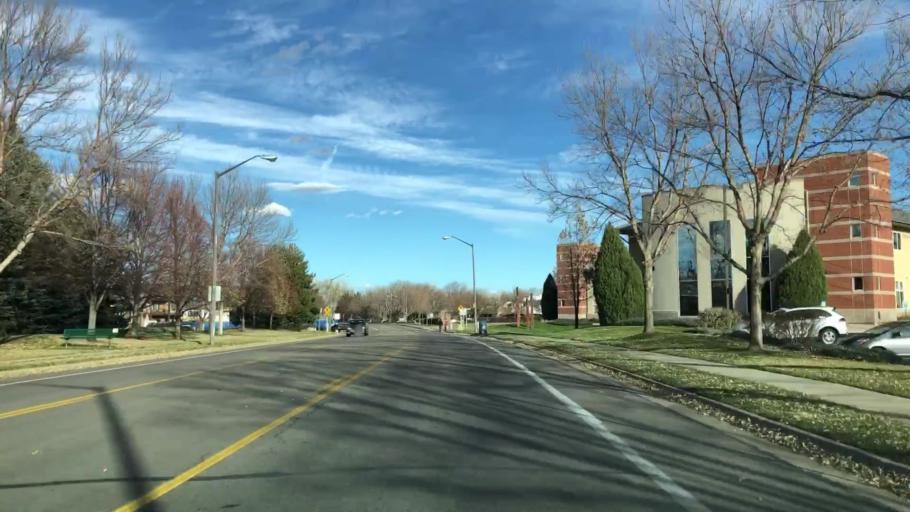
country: US
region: Colorado
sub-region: Larimer County
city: Fort Collins
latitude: 40.5556
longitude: -105.0925
